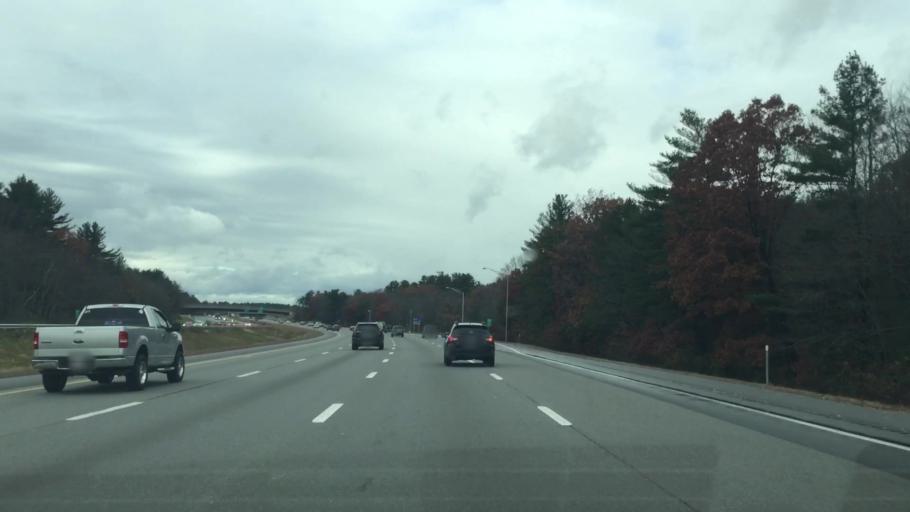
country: US
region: Massachusetts
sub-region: Essex County
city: Methuen
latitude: 42.7516
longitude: -71.2181
